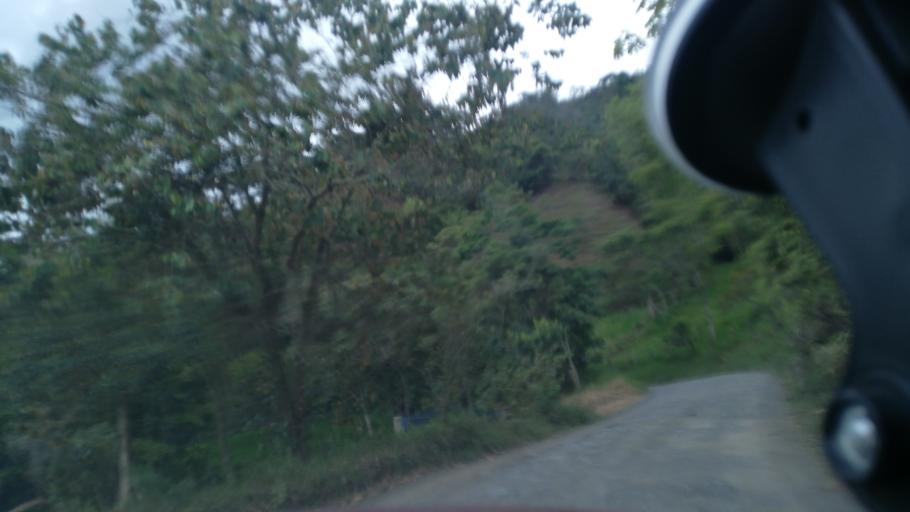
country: CO
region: Cundinamarca
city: Pacho
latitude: 5.1661
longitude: -74.2204
